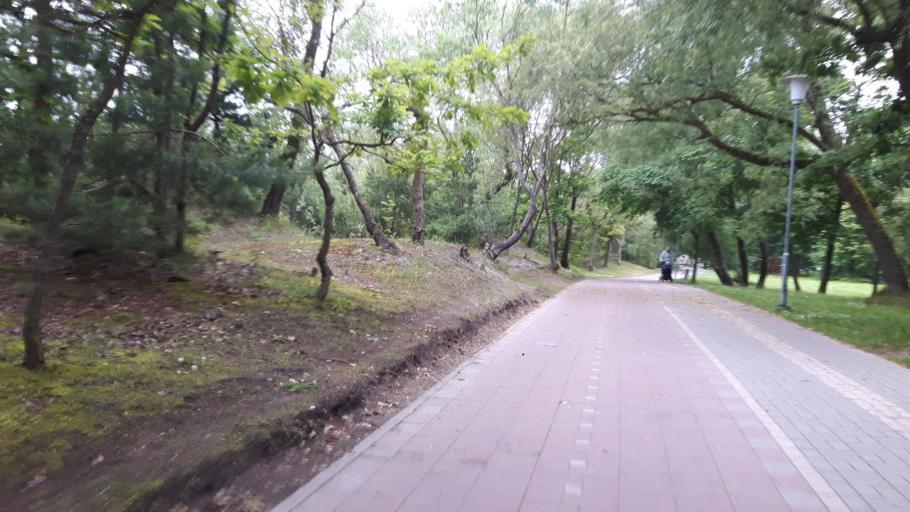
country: LV
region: Liepaja
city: Liepaja
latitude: 56.4983
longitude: 20.9958
